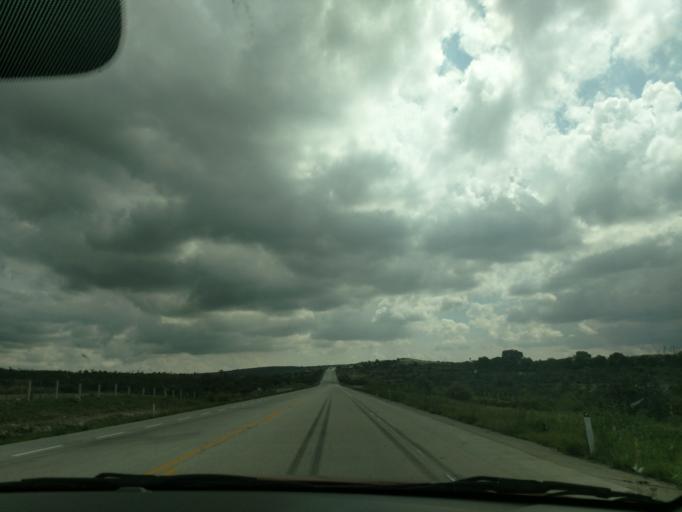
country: MX
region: Jalisco
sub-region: Ojuelos de Jalisco
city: Matanzas
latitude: 21.5587
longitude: -101.6888
